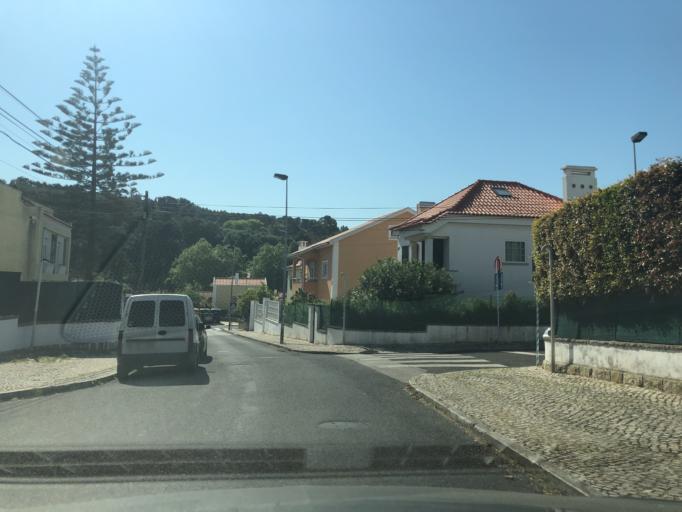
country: PT
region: Lisbon
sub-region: Oeiras
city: Terrugem
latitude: 38.7070
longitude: -9.2751
